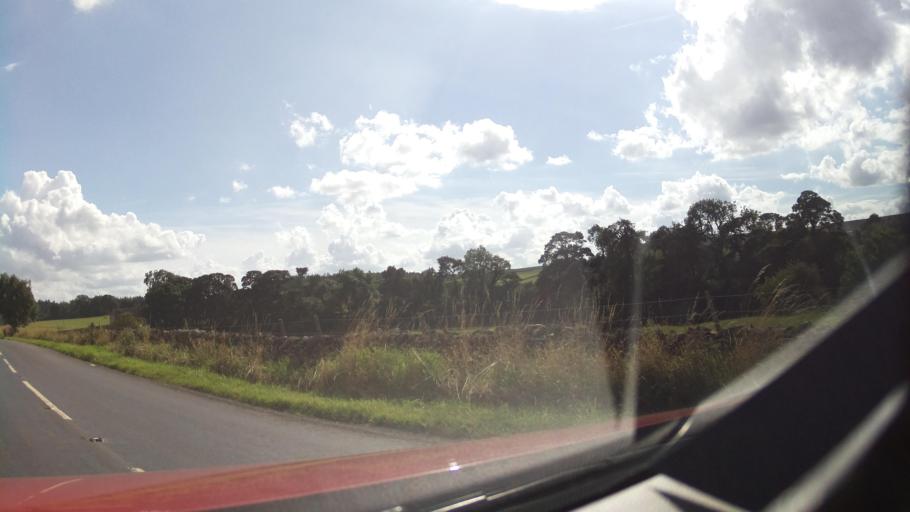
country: GB
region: England
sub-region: North Yorkshire
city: Leyburn
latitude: 54.3627
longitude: -1.8196
